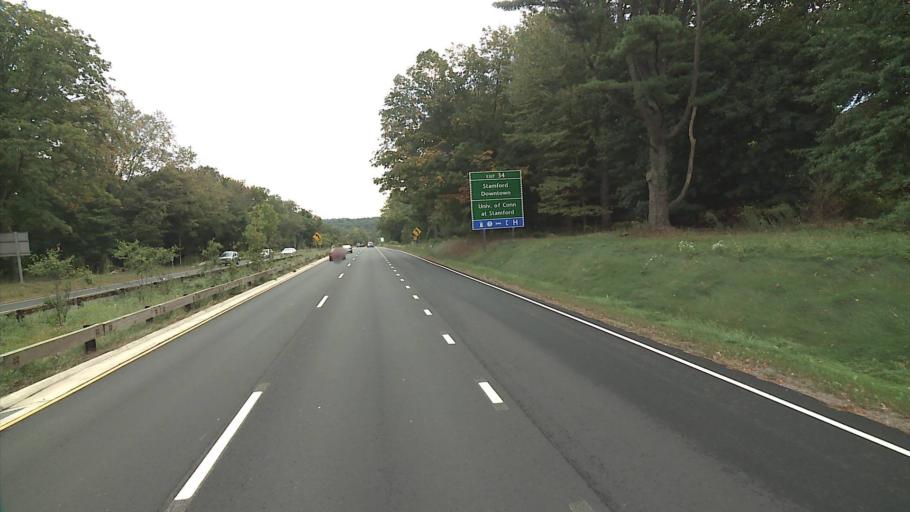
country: US
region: Connecticut
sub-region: Fairfield County
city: North Stamford
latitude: 41.1010
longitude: -73.5751
